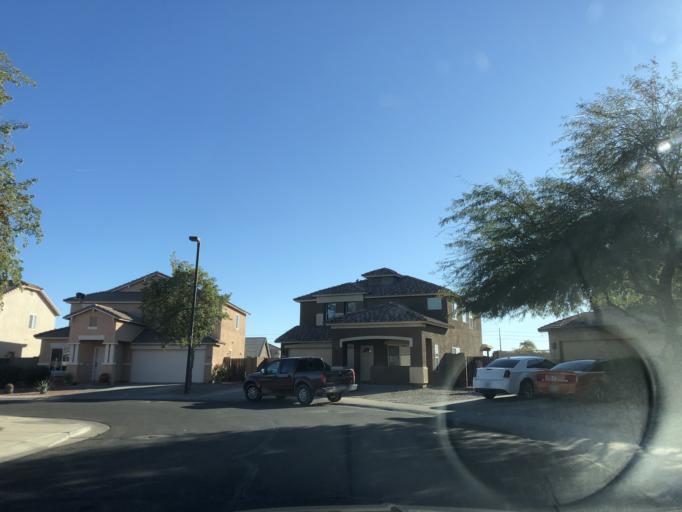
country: US
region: Arizona
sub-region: Maricopa County
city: Buckeye
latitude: 33.4377
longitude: -112.5732
